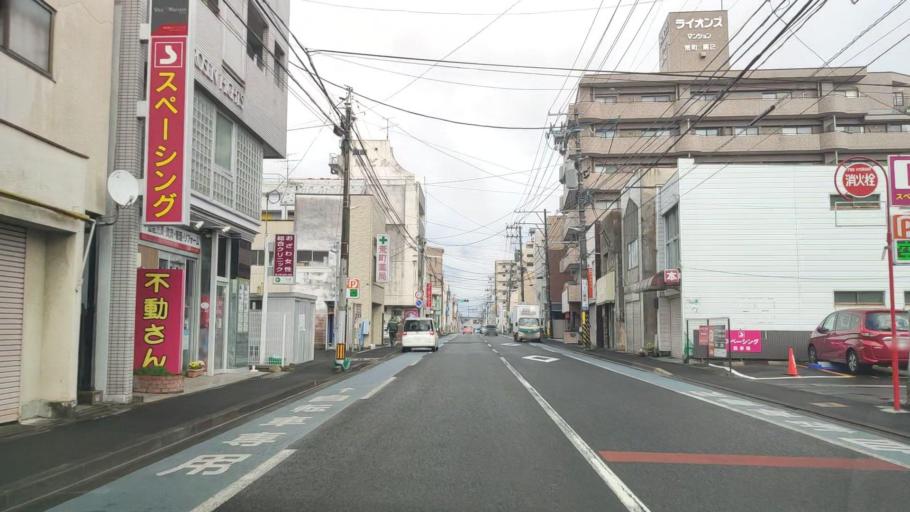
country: JP
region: Miyagi
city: Sendai
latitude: 38.2488
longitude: 140.8849
